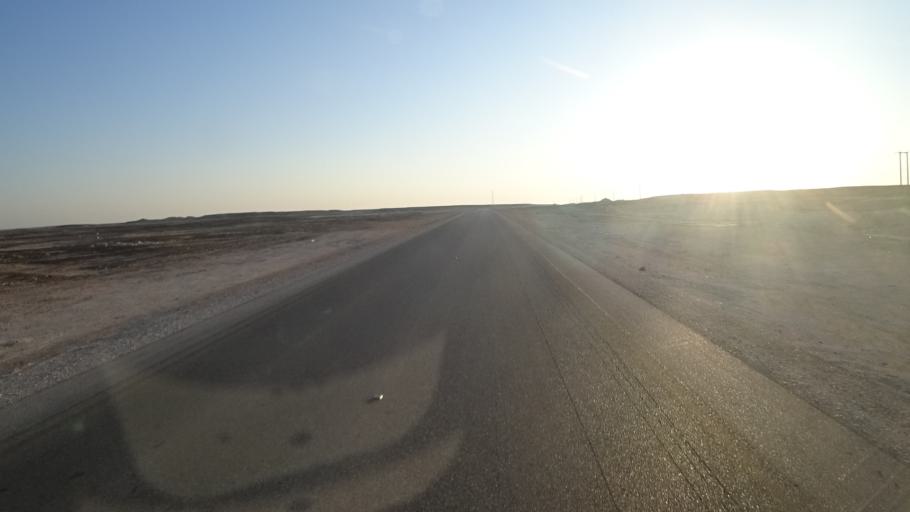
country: OM
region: Zufar
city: Salalah
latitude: 17.5480
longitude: 53.4256
